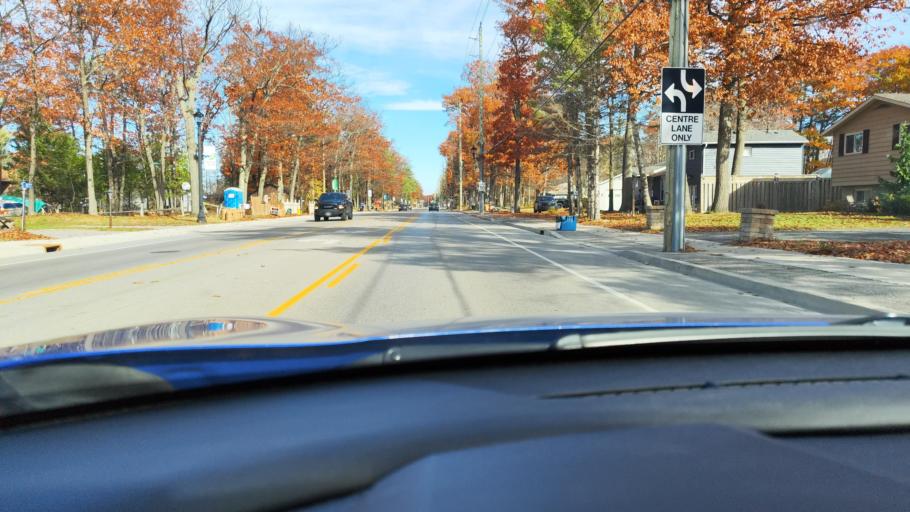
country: CA
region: Ontario
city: Wasaga Beach
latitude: 44.4966
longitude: -80.0414
